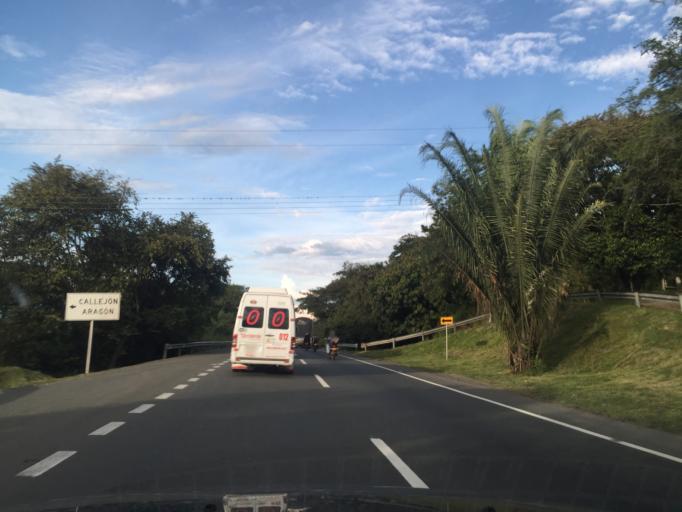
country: CO
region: Valle del Cauca
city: Bugalagrande
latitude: 4.2399
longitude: -76.1271
